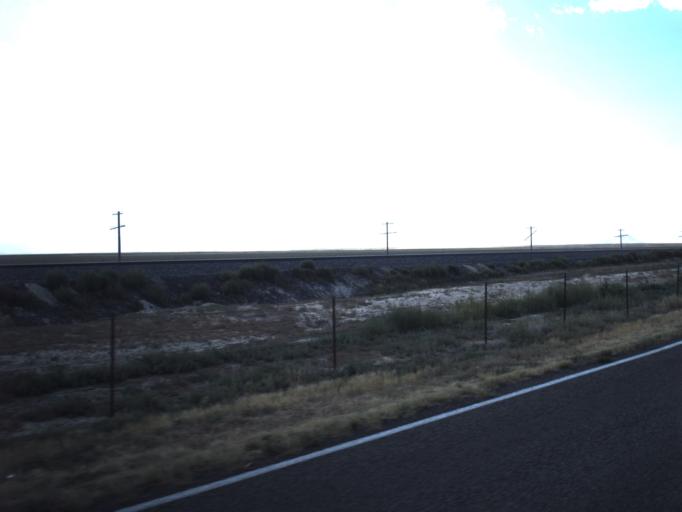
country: US
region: Utah
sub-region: Millard County
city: Delta
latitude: 39.0092
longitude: -112.7839
